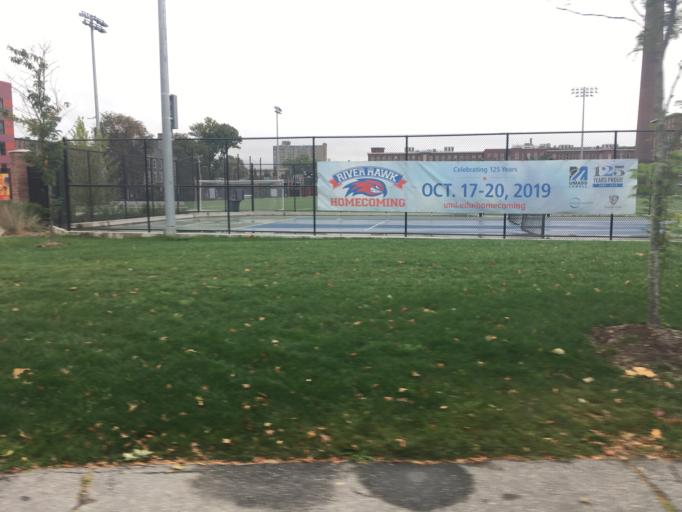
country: US
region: Massachusetts
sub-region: Middlesex County
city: Lowell
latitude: 42.6514
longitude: -71.3185
